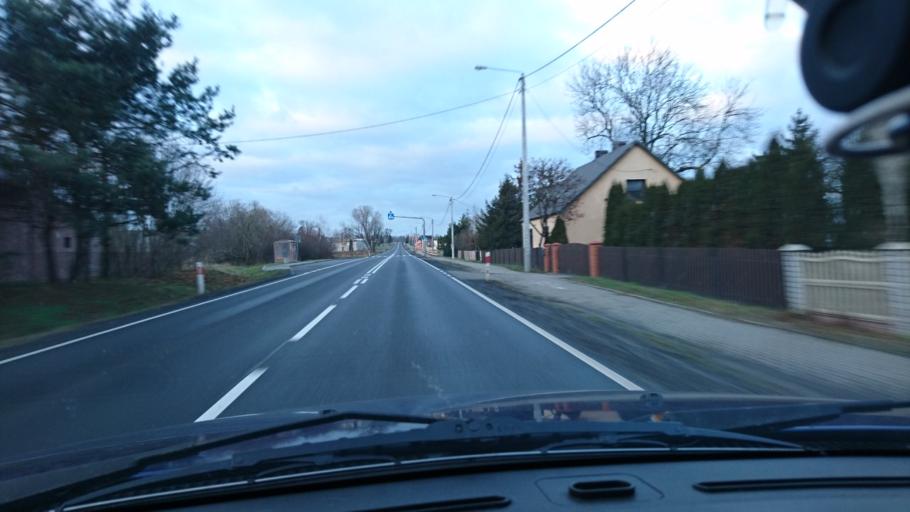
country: PL
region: Greater Poland Voivodeship
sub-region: Powiat ostrzeszowski
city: Ostrzeszow
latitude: 51.3540
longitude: 17.9473
